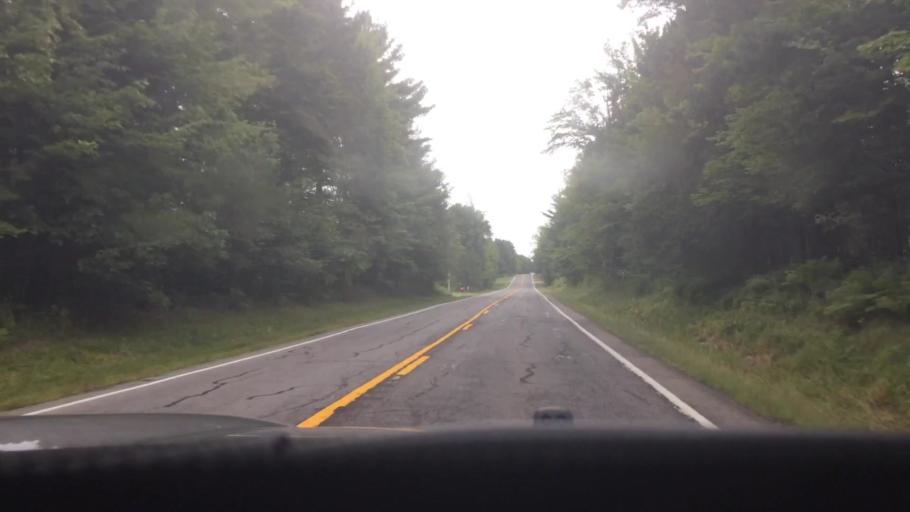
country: US
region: New York
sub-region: St. Lawrence County
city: Hannawa Falls
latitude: 44.6664
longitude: -74.7401
